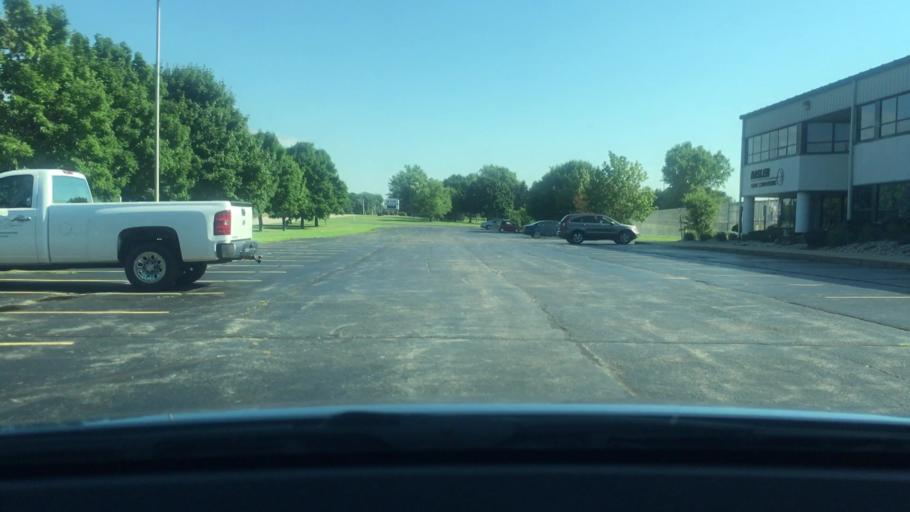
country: US
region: Wisconsin
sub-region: Winnebago County
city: Oshkosh
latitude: 43.9733
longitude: -88.5434
